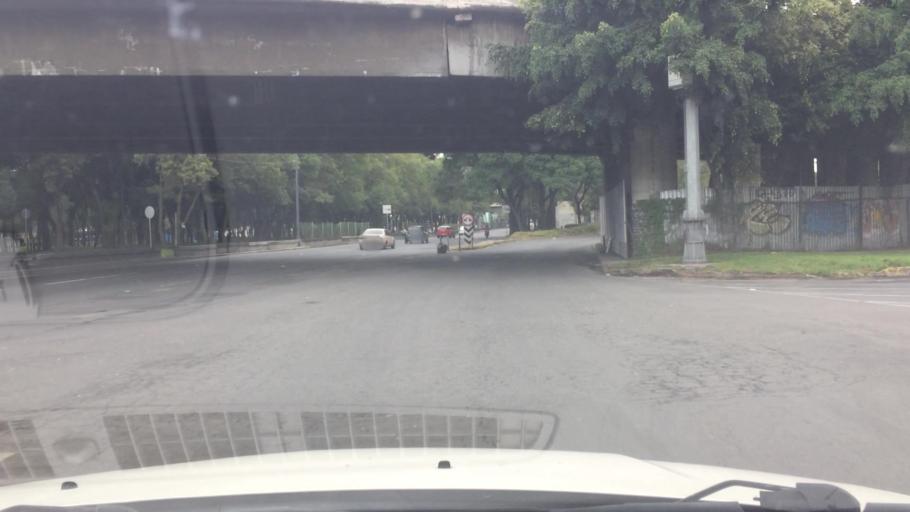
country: MX
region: Mexico City
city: Xochimilco
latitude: 19.2855
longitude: -99.1247
